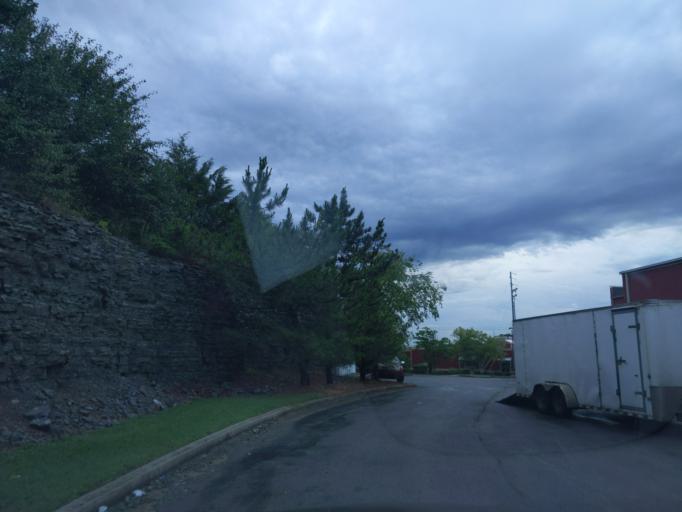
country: US
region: Tennessee
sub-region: Williamson County
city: Brentwood Estates
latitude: 36.0392
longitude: -86.7460
